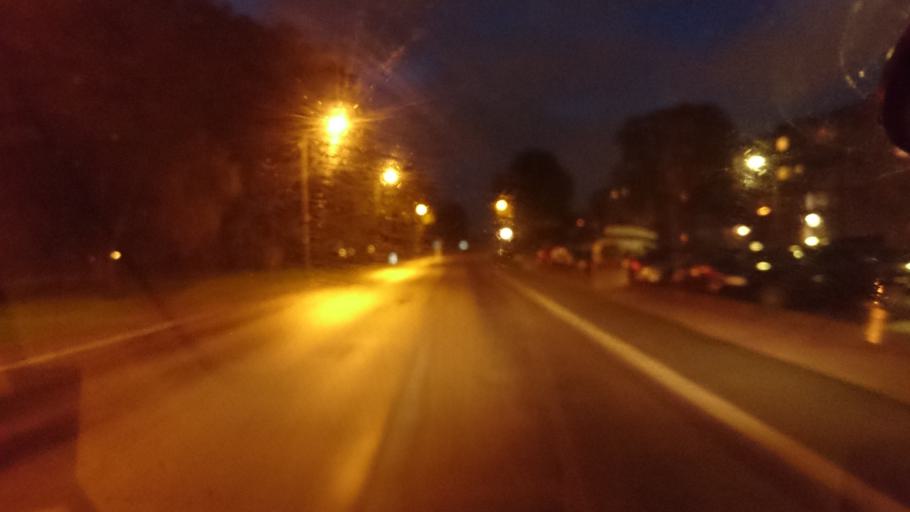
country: SE
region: Vaestra Goetaland
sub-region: Goteborg
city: Majorna
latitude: 57.6744
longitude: 11.9126
